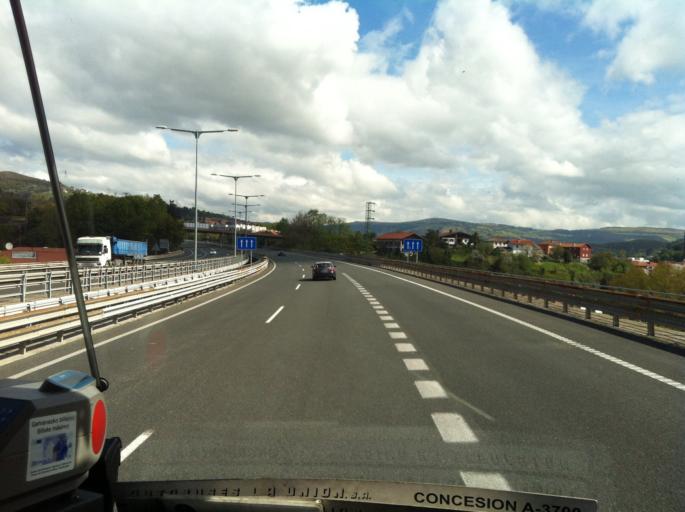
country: ES
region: Basque Country
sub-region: Bizkaia
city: Arrigorriaga
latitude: 43.2028
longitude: -2.8927
